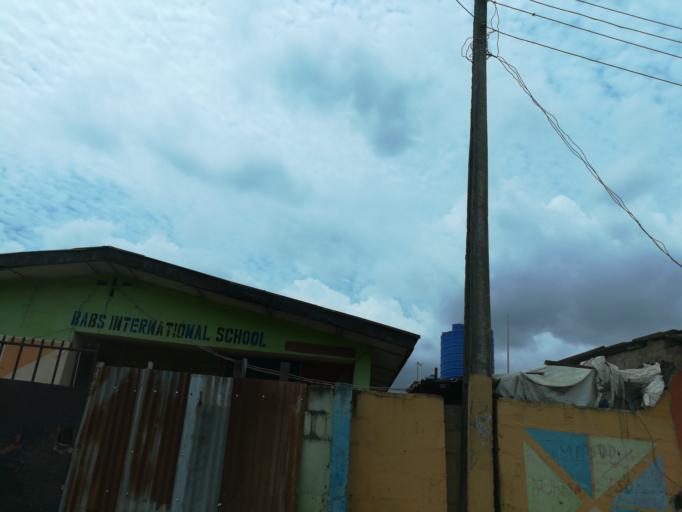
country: NG
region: Lagos
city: Oshodi
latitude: 6.5599
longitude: 3.3287
